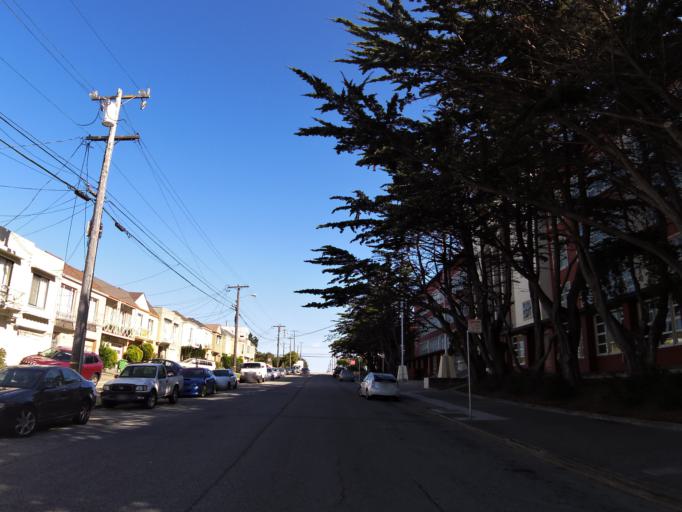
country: US
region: California
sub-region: San Mateo County
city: Daly City
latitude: 37.7469
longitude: -122.4813
